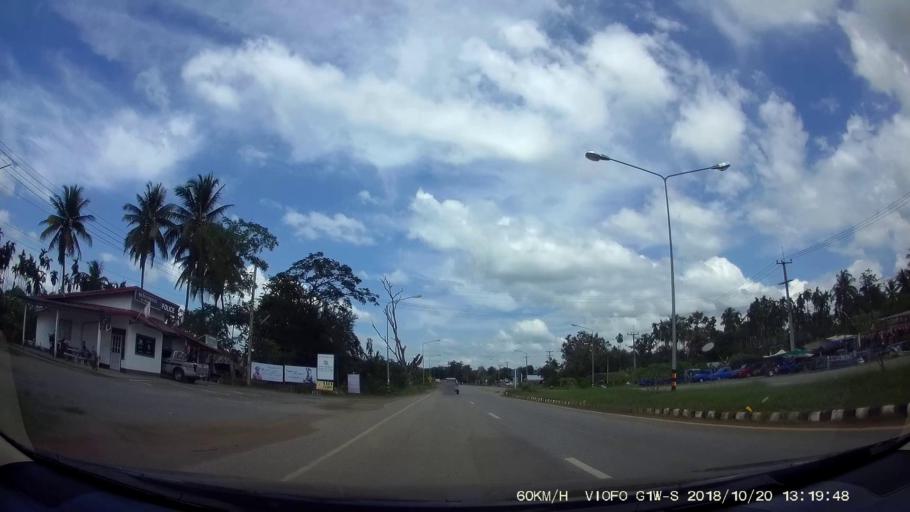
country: TH
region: Chaiyaphum
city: Khon San
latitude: 16.5421
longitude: 101.9011
